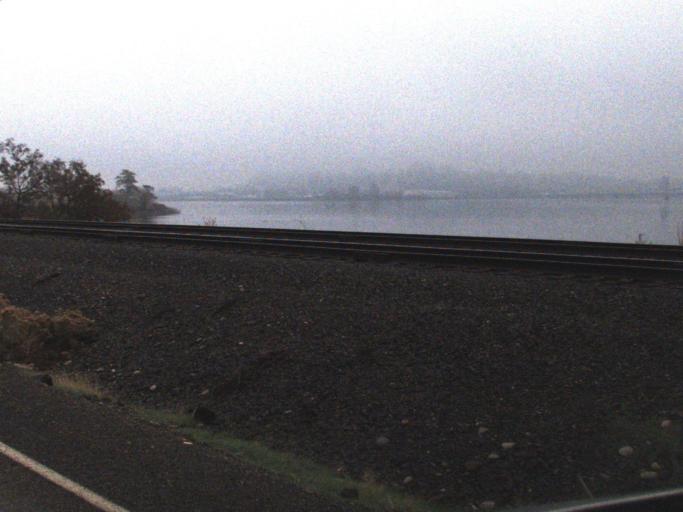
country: US
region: Washington
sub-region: Asotin County
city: Clarkston
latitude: 46.4318
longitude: -117.0426
